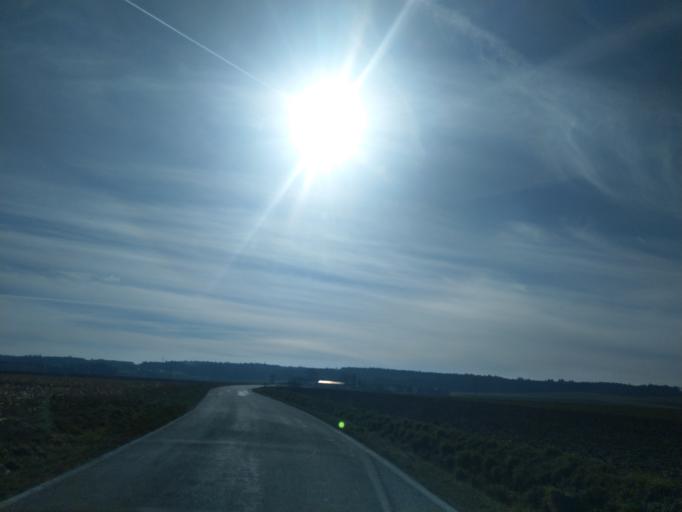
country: DE
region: Bavaria
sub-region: Lower Bavaria
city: Buchhofen
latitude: 48.6738
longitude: 12.9355
